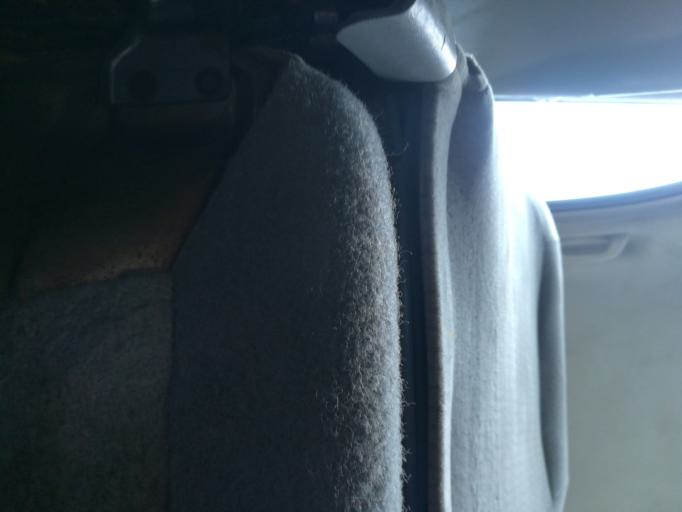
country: NG
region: Lagos
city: Ikoyi
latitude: 6.4436
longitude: 3.4237
